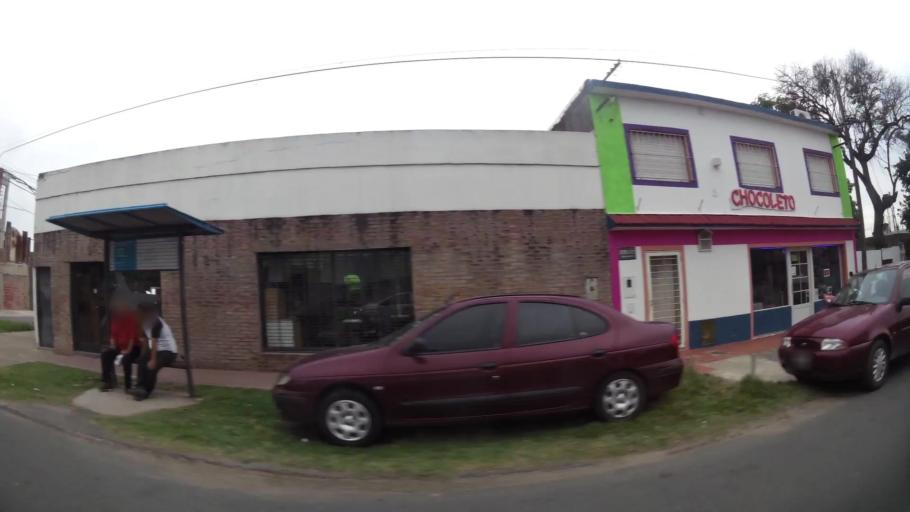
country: AR
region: Santa Fe
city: Granadero Baigorria
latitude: -32.8963
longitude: -60.7014
